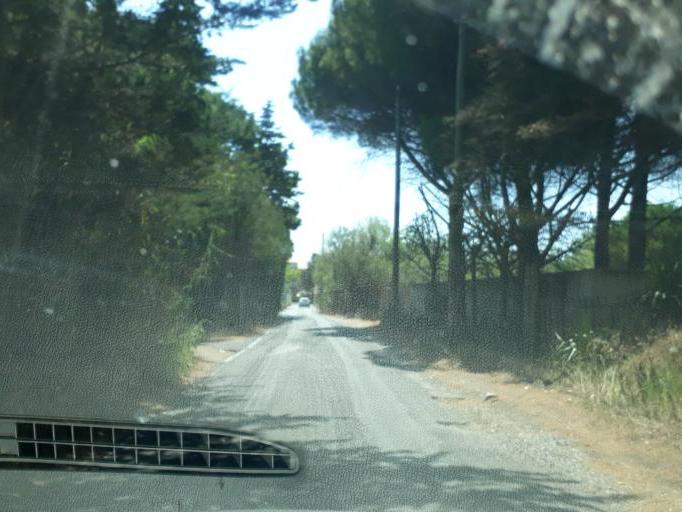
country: FR
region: Languedoc-Roussillon
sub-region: Departement de l'Herault
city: Le Cap d'Agde
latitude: 43.2818
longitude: 3.4911
